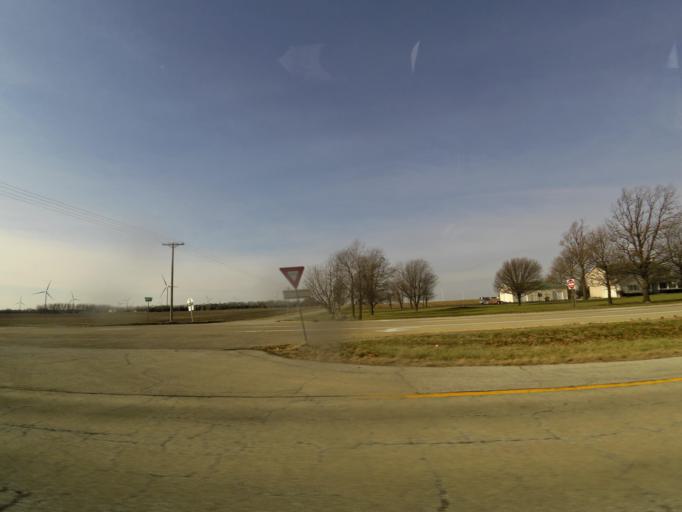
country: US
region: Illinois
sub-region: Macon County
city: Maroa
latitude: 39.9934
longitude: -88.9561
